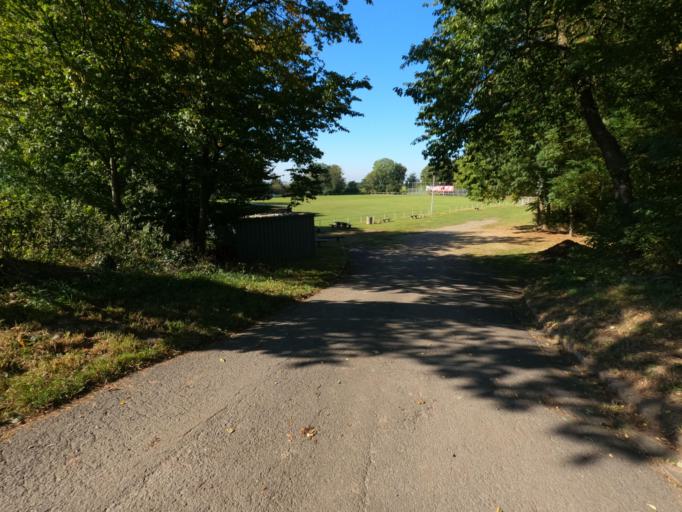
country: DE
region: North Rhine-Westphalia
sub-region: Regierungsbezirk Koln
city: Linnich
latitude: 50.9864
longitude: 6.3022
